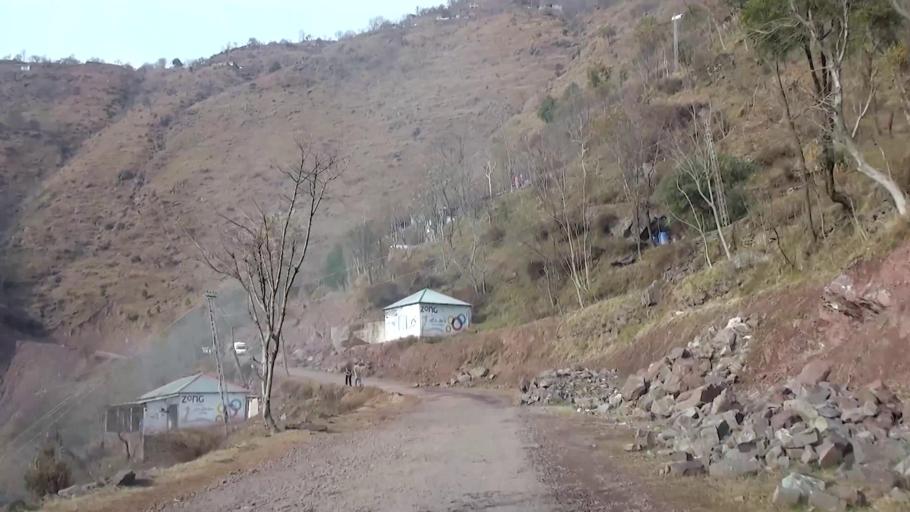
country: PK
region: Azad Kashmir
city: Muzaffarabad
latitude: 34.3688
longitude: 73.5251
